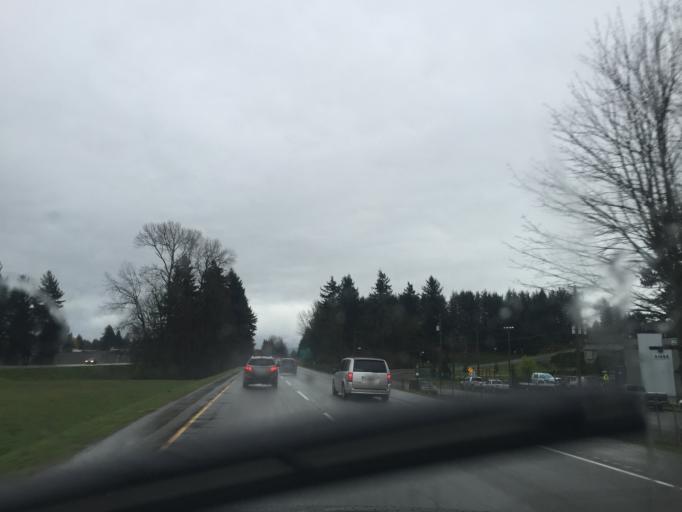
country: US
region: Washington
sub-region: Whatcom County
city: Sumas
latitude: 49.0455
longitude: -122.3532
